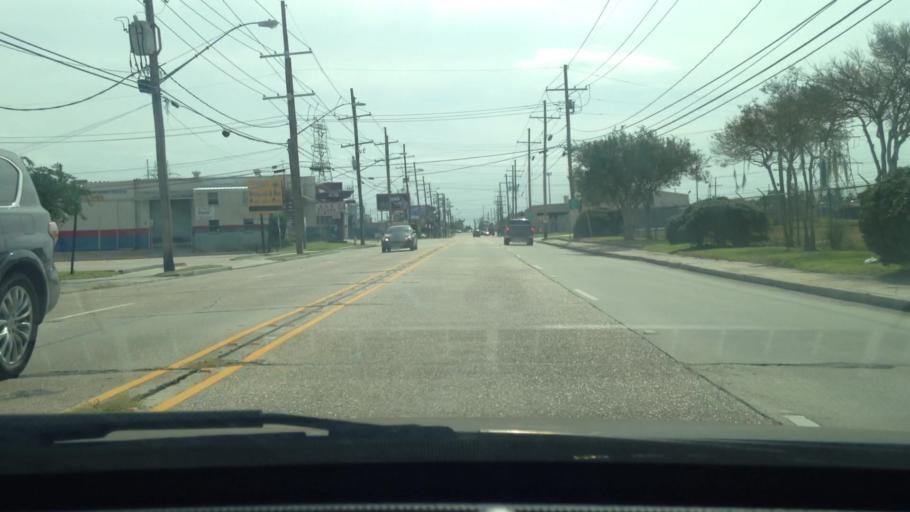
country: US
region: Louisiana
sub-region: Jefferson Parish
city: River Ridge
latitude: 29.9817
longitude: -90.2123
